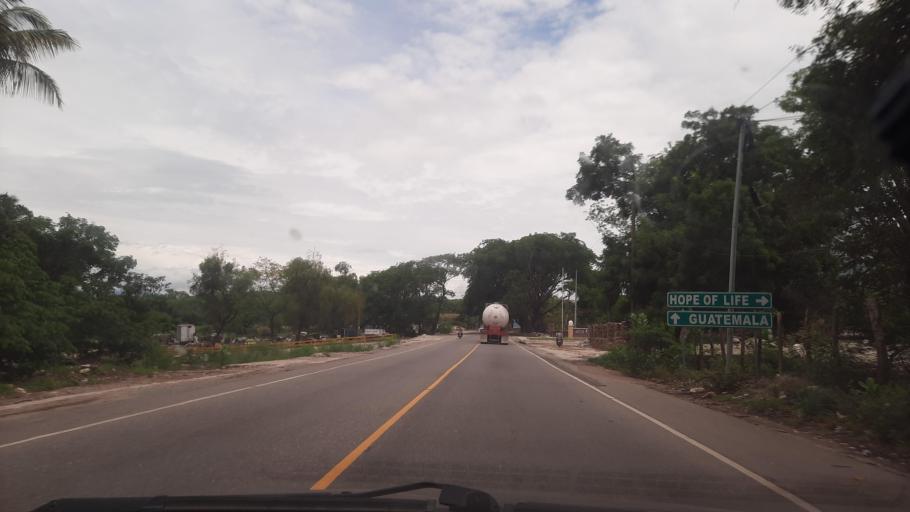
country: GT
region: Zacapa
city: Rio Hondo
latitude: 15.0722
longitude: -89.5070
